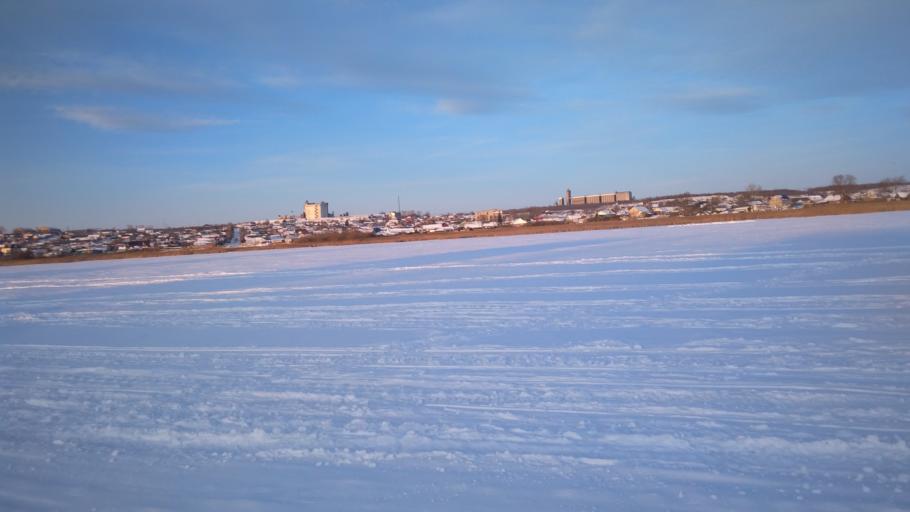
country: RU
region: Chelyabinsk
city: Troitsk
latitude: 54.0885
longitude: 61.5829
